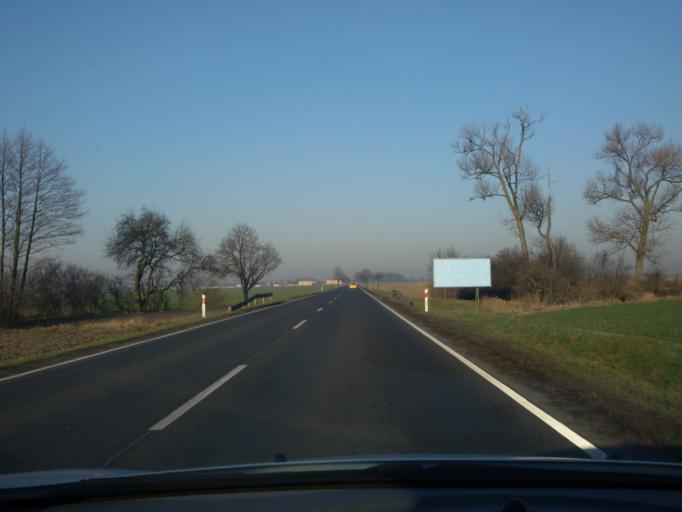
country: PL
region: Greater Poland Voivodeship
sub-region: Powiat leszczynski
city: Swieciechowa
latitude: 51.8248
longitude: 16.4666
